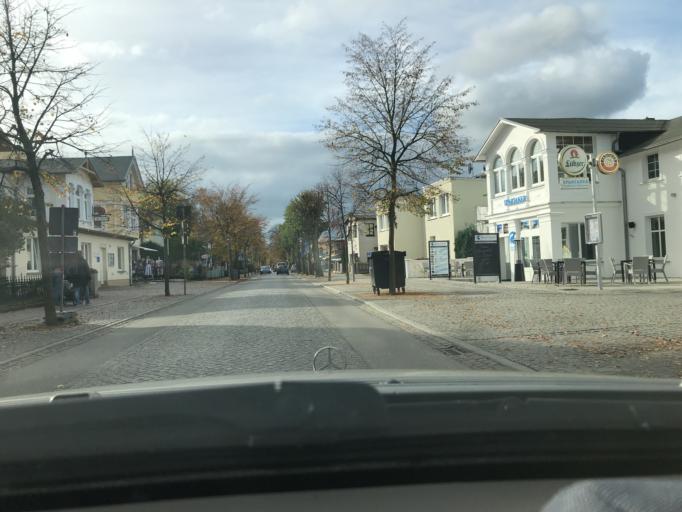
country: DE
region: Mecklenburg-Vorpommern
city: Ostseebad Zinnowitz
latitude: 54.0781
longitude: 13.9113
